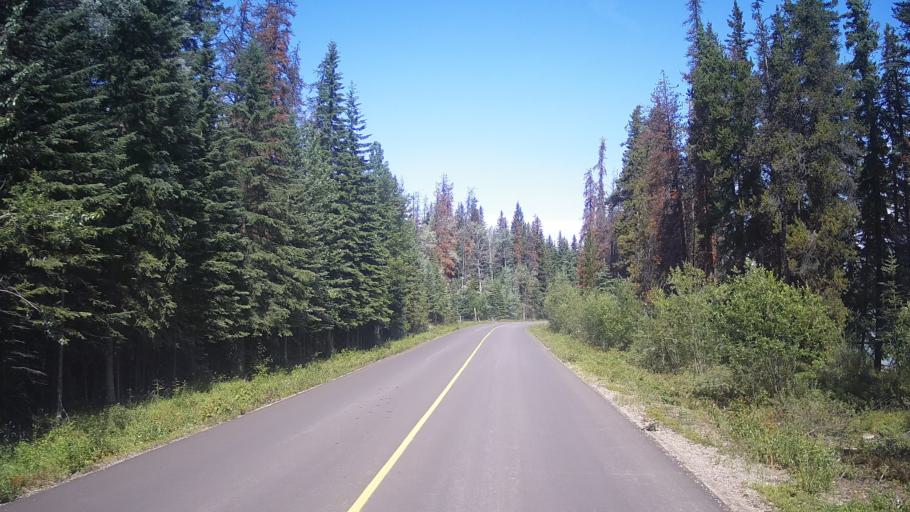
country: CA
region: Alberta
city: Jasper Park Lodge
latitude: 52.7441
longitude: -117.9697
